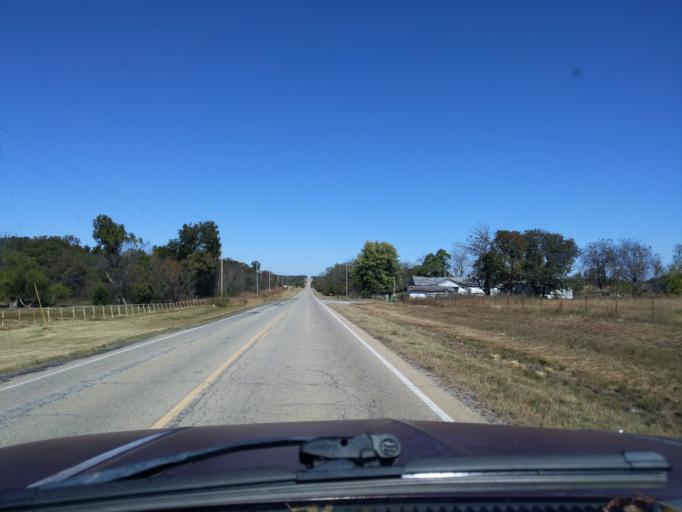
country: US
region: Oklahoma
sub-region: Creek County
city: Bristow
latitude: 35.7220
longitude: -96.3872
